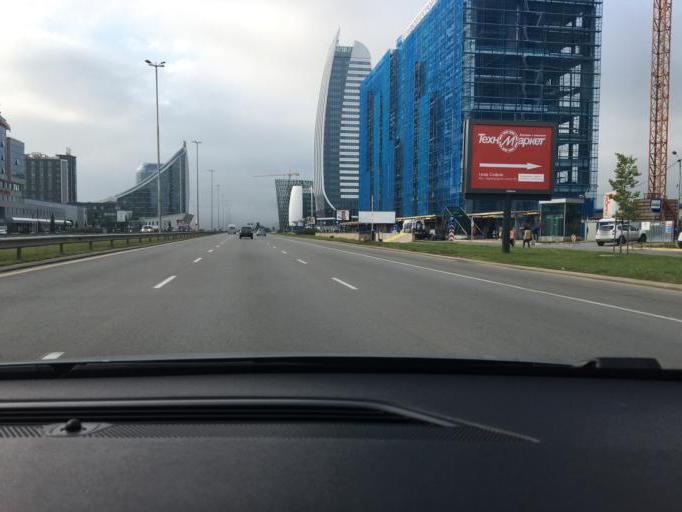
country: BG
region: Sofia-Capital
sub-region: Stolichna Obshtina
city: Sofia
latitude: 42.6499
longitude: 23.3932
